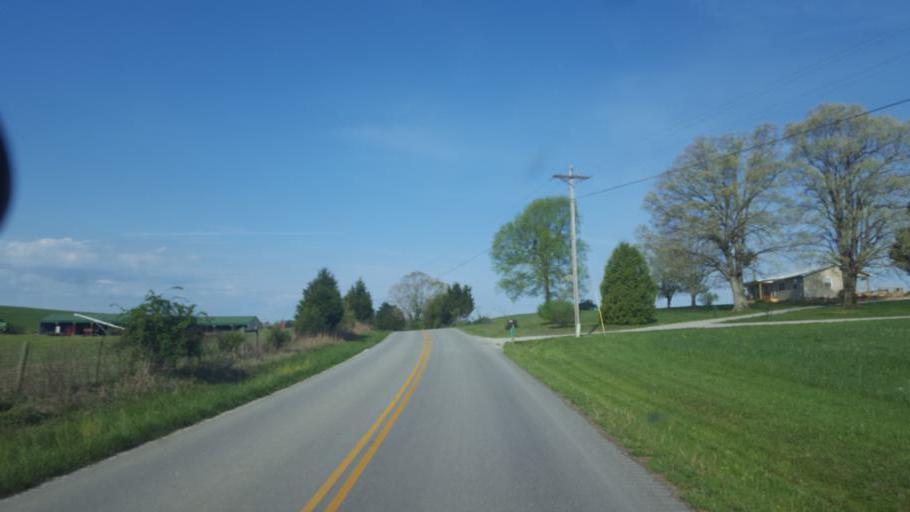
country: US
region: Kentucky
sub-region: Hart County
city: Munfordville
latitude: 37.3188
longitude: -86.0958
